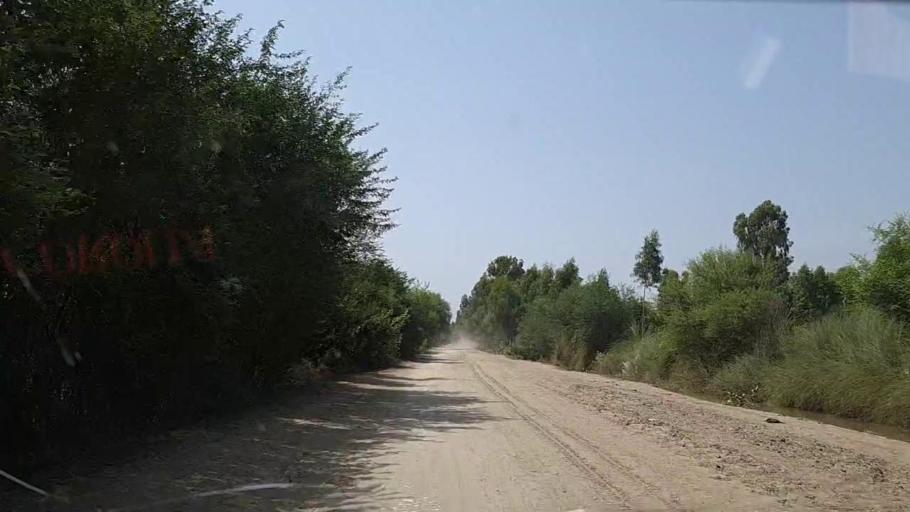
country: PK
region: Sindh
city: Ghotki
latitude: 28.0874
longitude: 69.3366
